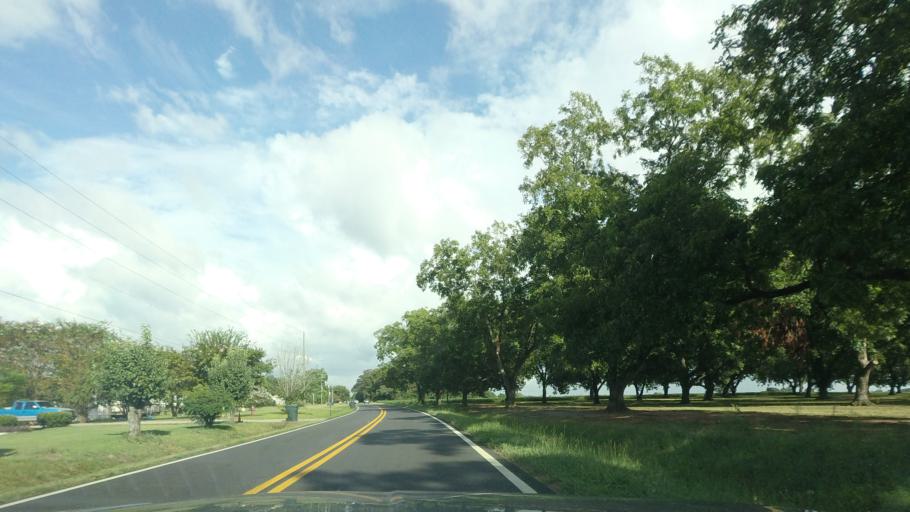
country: US
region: Georgia
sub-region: Peach County
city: Byron
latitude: 32.6351
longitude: -83.7279
